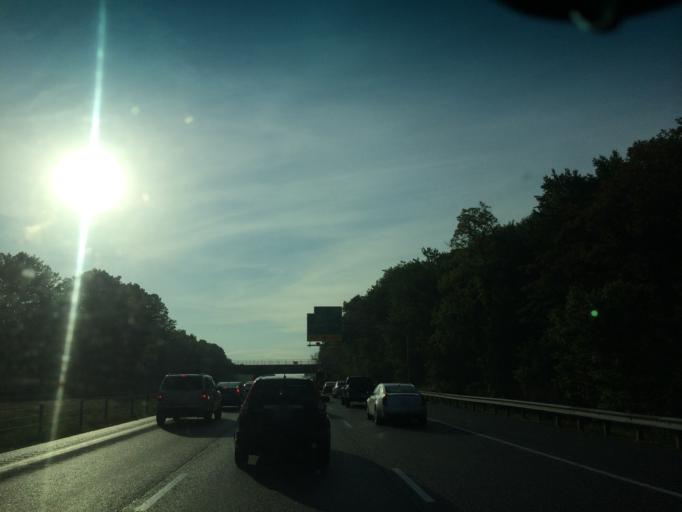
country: US
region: Maryland
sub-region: Carroll County
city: Sykesville
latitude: 39.3066
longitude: -76.9328
